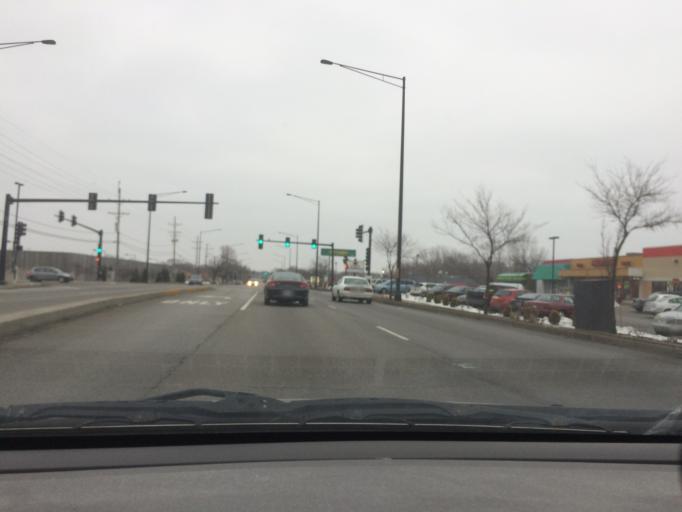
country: US
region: Illinois
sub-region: DuPage County
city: Hanover Park
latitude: 42.0051
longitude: -88.1436
